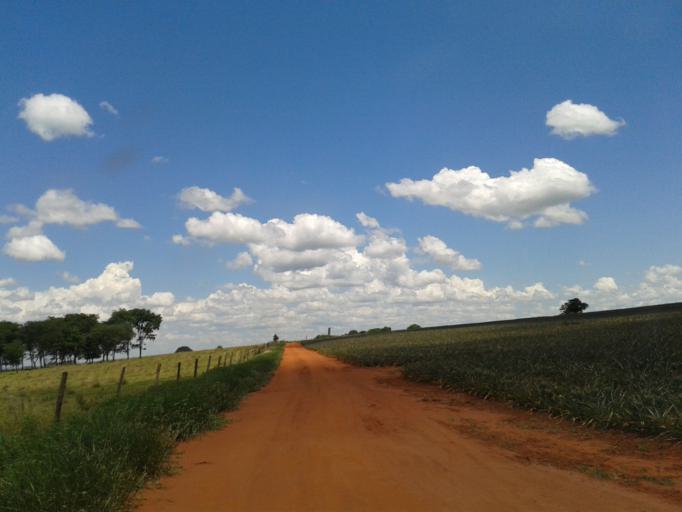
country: BR
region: Minas Gerais
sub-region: Centralina
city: Centralina
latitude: -18.6969
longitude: -49.1583
